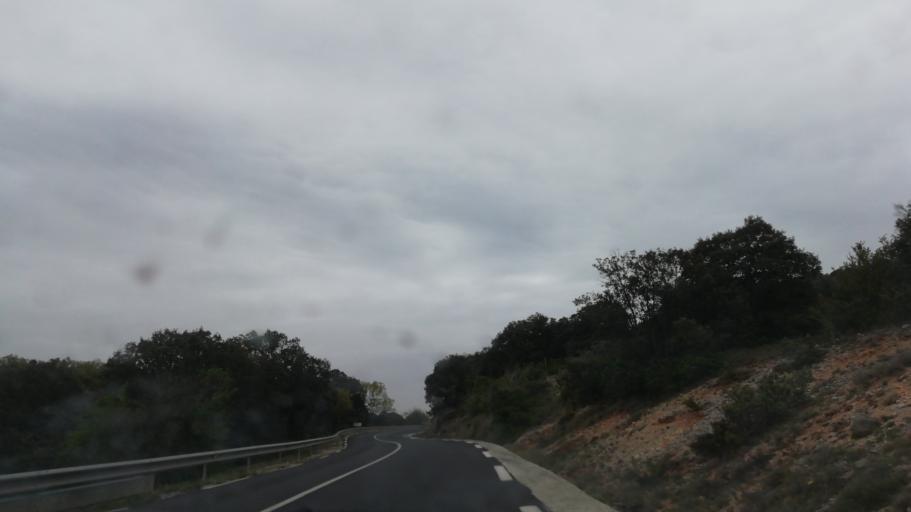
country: FR
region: Languedoc-Roussillon
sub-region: Departement de l'Herault
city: Saint-Martin-de-Londres
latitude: 43.7715
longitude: 3.7250
